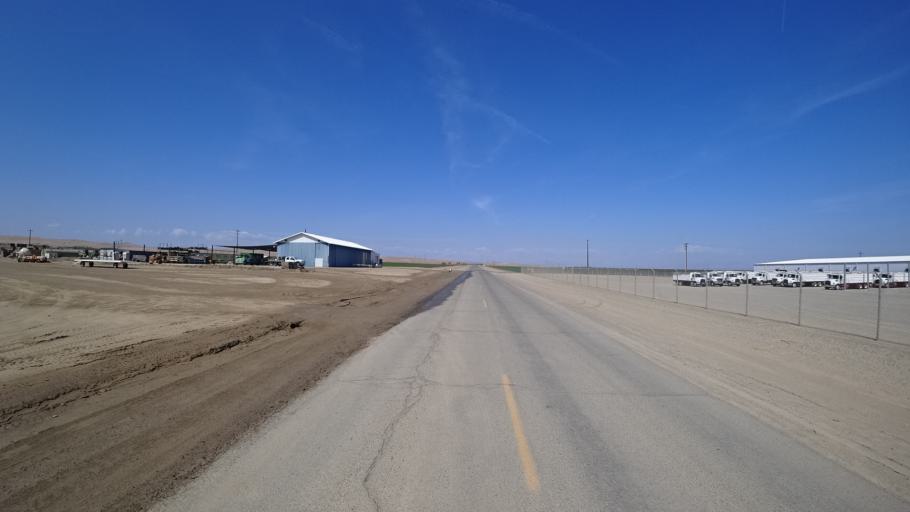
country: US
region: California
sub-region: Kings County
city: Avenal
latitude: 36.0725
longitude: -120.0472
